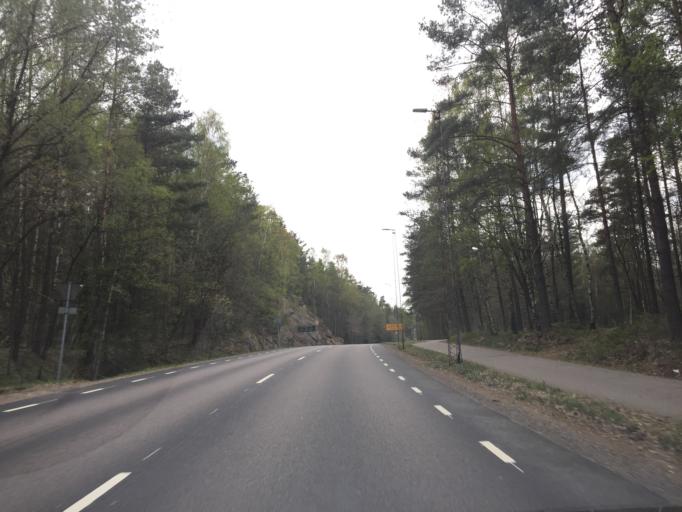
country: SE
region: Vaestra Goetaland
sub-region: Goteborg
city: Rannebergen
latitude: 57.8051
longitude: 12.0608
